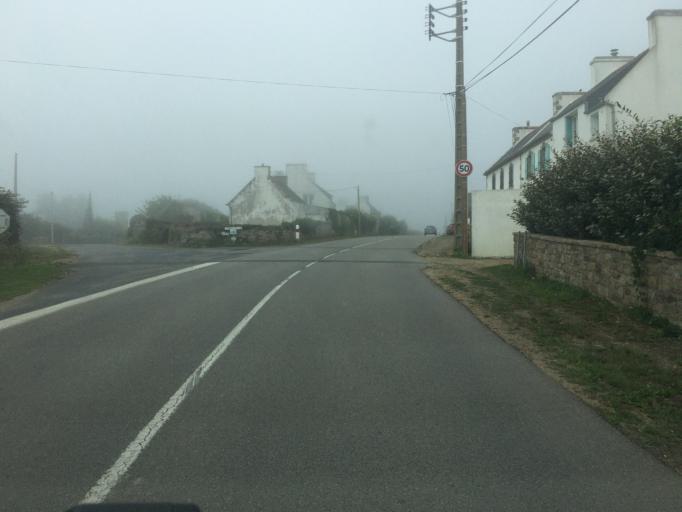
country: FR
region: Brittany
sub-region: Departement du Finistere
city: Plogoff
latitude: 48.0628
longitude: -4.6253
